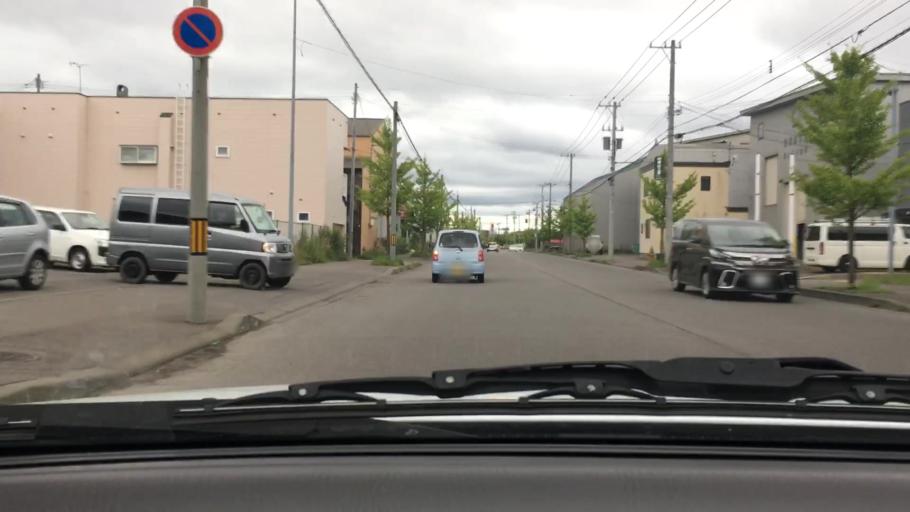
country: JP
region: Hokkaido
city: Hakodate
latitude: 41.7987
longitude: 140.7244
